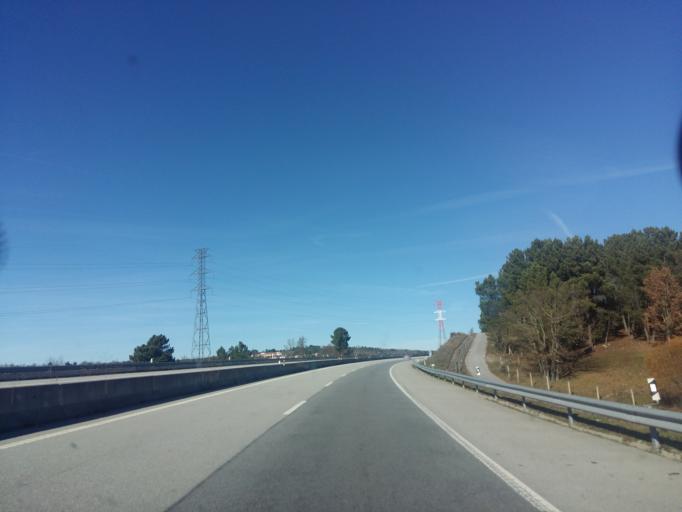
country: PT
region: Guarda
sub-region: Guarda
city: Sequeira
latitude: 40.5500
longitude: -7.2170
